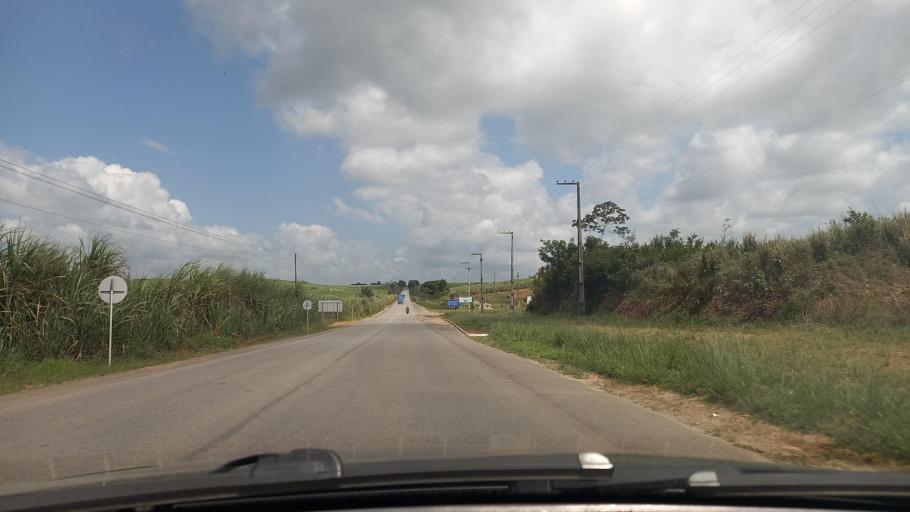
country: BR
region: Pernambuco
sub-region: Goiana
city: Goiana
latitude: -7.5708
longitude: -35.0285
